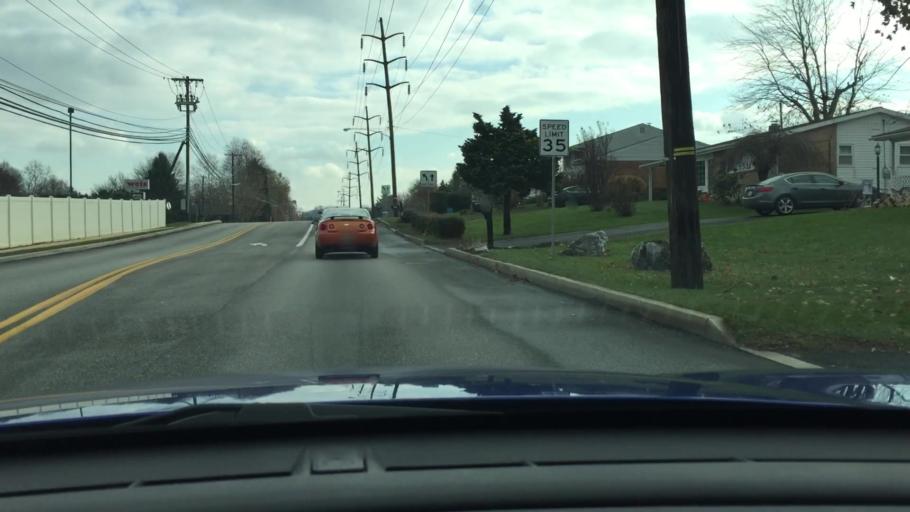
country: US
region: Pennsylvania
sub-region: Cumberland County
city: Shiremanstown
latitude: 40.2173
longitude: -76.9763
